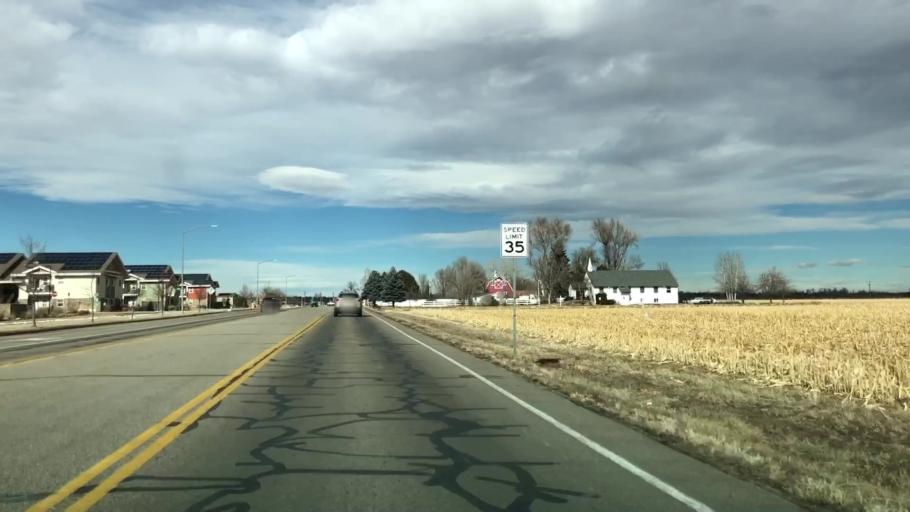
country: US
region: Colorado
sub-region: Weld County
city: Windsor
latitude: 40.4874
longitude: -104.9264
